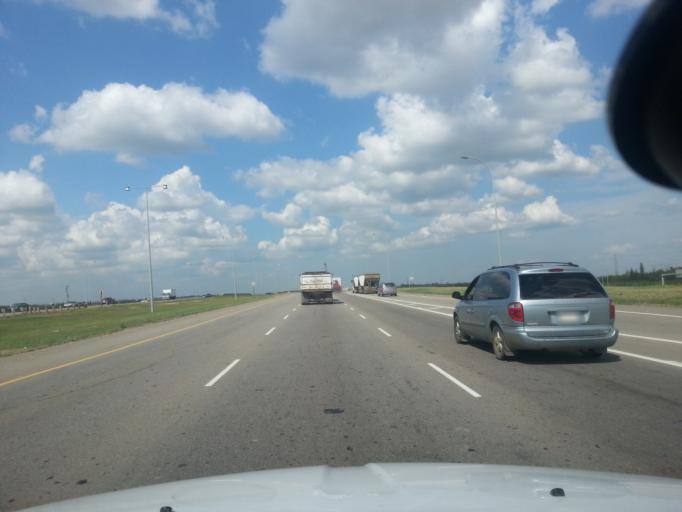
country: CA
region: Alberta
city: St. Albert
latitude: 53.5388
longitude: -113.6588
